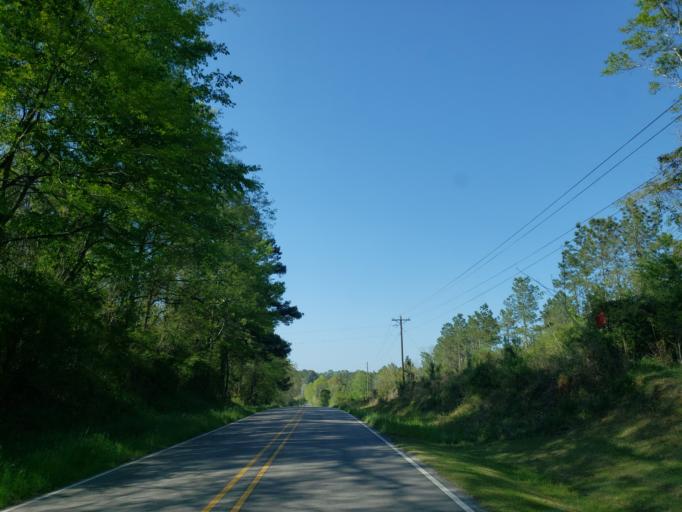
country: US
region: Mississippi
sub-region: Forrest County
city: Rawls Springs
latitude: 31.5466
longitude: -89.3653
